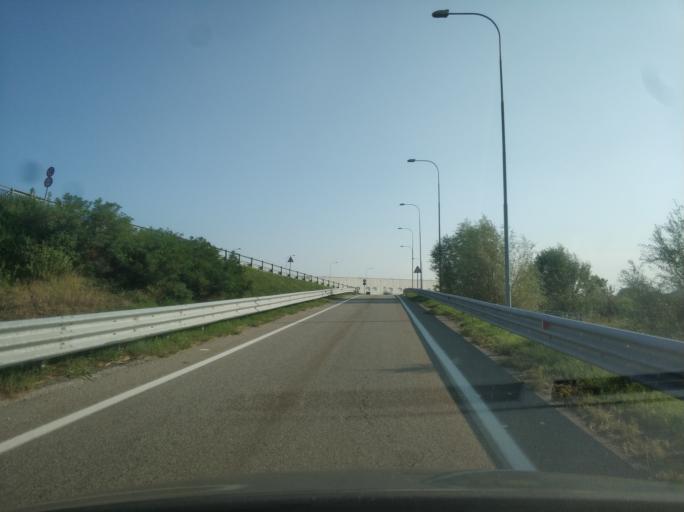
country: IT
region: Piedmont
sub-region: Provincia di Cuneo
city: Roreto
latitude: 44.6662
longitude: 7.8227
